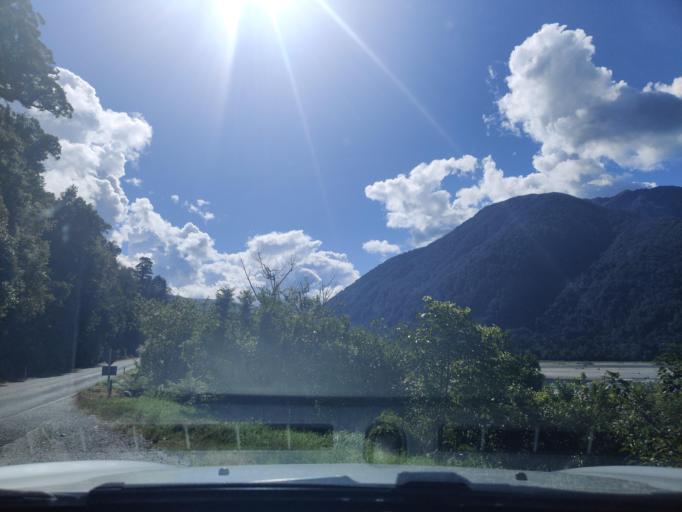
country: NZ
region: Otago
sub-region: Queenstown-Lakes District
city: Wanaka
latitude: -43.9455
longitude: 169.1476
